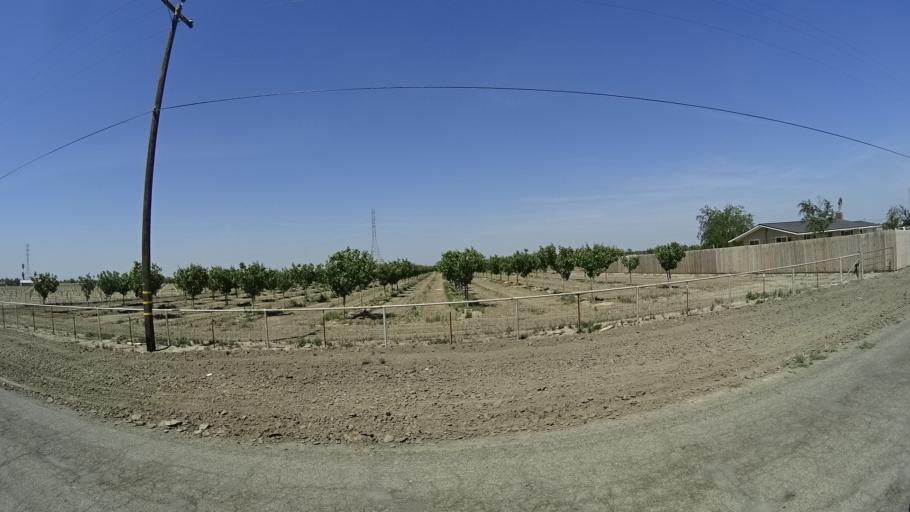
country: US
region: California
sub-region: Fresno County
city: Riverdale
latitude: 36.3913
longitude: -119.8872
